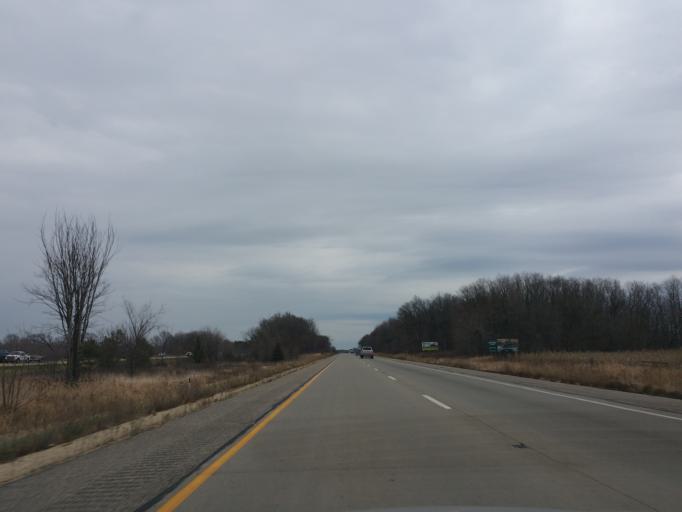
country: US
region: Wisconsin
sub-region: Juneau County
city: New Lisbon
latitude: 43.9003
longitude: -90.1933
